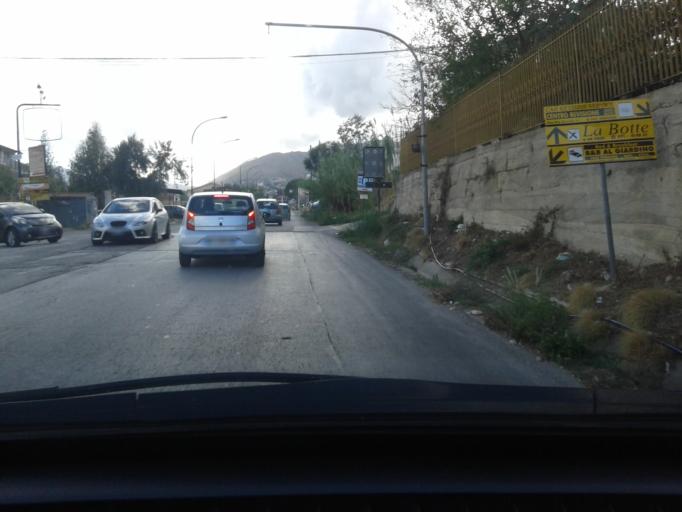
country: IT
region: Sicily
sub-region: Palermo
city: Monreale
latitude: 38.0795
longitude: 13.2978
